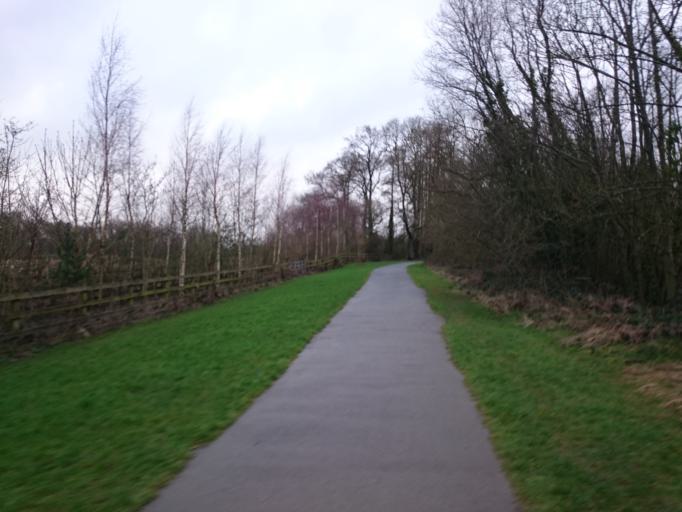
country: IE
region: Leinster
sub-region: Kilkenny
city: Kilkenny
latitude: 52.6730
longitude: -7.2610
